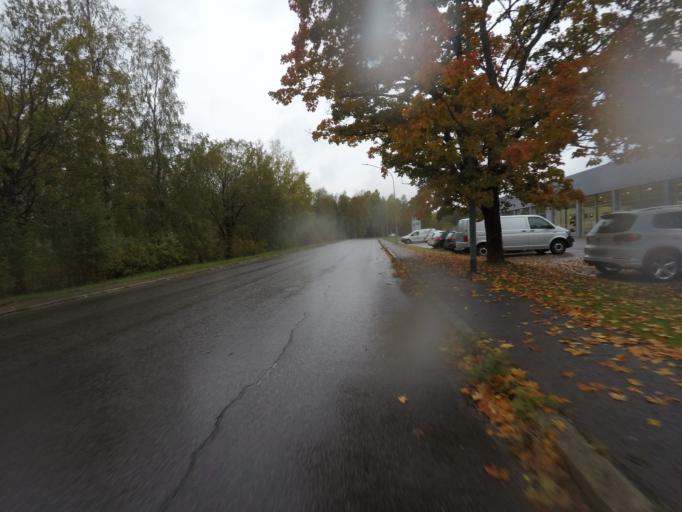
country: SE
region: OErebro
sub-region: Karlskoga Kommun
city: Karlskoga
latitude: 59.3248
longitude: 14.4833
